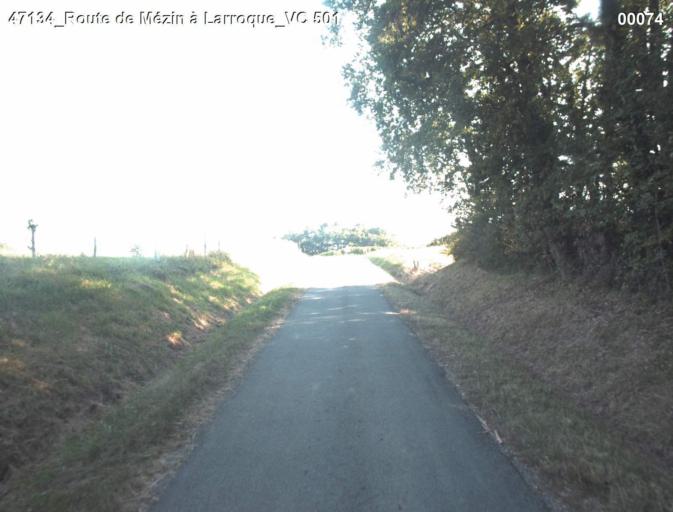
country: FR
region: Aquitaine
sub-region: Departement du Lot-et-Garonne
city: Mezin
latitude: 43.9994
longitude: 0.2774
